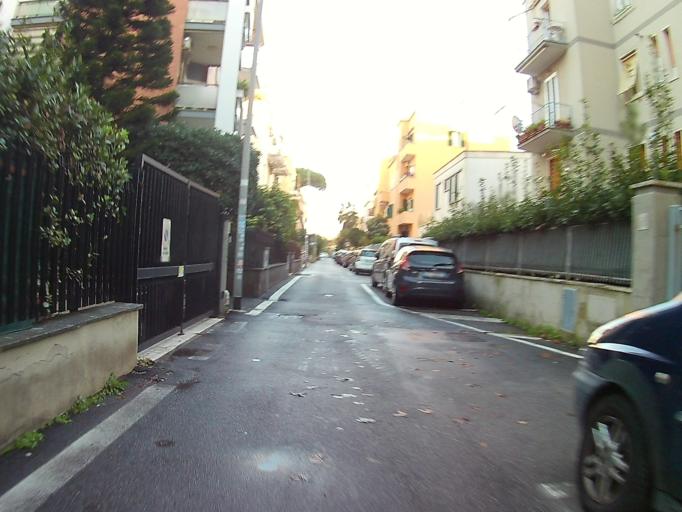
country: IT
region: Latium
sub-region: Citta metropolitana di Roma Capitale
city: Lido di Ostia
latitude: 41.7297
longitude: 12.2821
